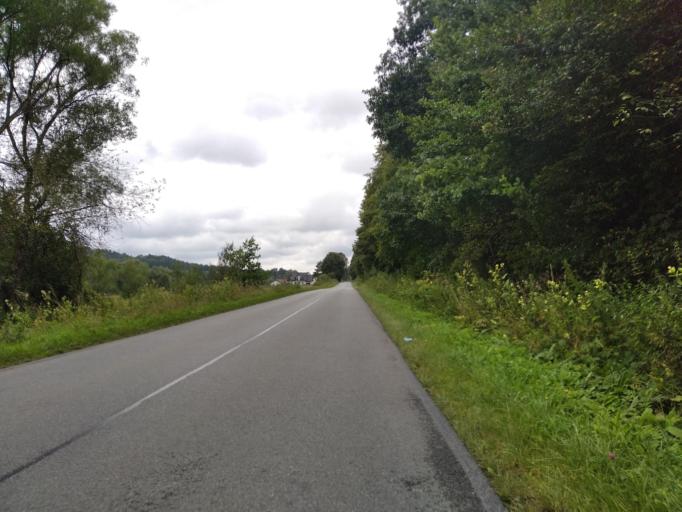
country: PL
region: Subcarpathian Voivodeship
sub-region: Powiat przemyski
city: Bircza
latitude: 49.6834
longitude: 22.4041
